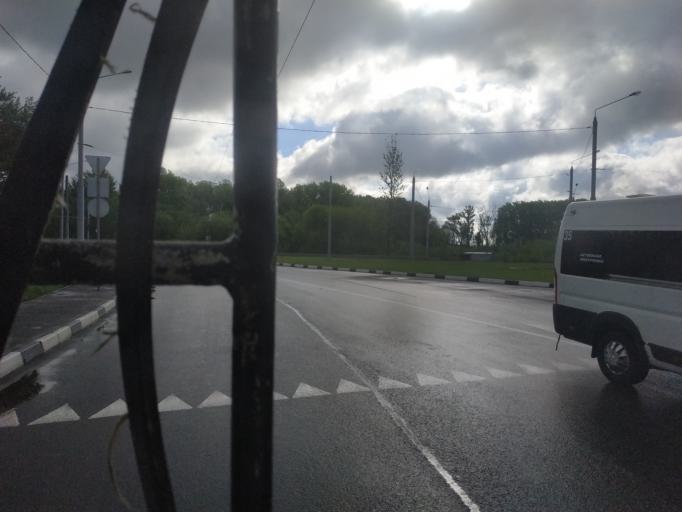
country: RU
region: Brjansk
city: Putevka
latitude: 53.2888
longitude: 34.3037
